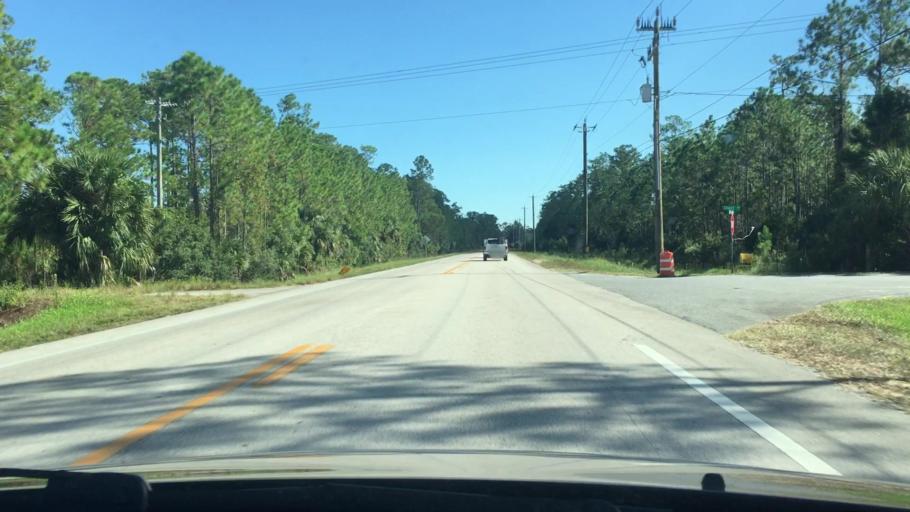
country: US
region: Florida
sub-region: Volusia County
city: Samsula-Spruce Creek
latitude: 29.1250
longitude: -81.0726
